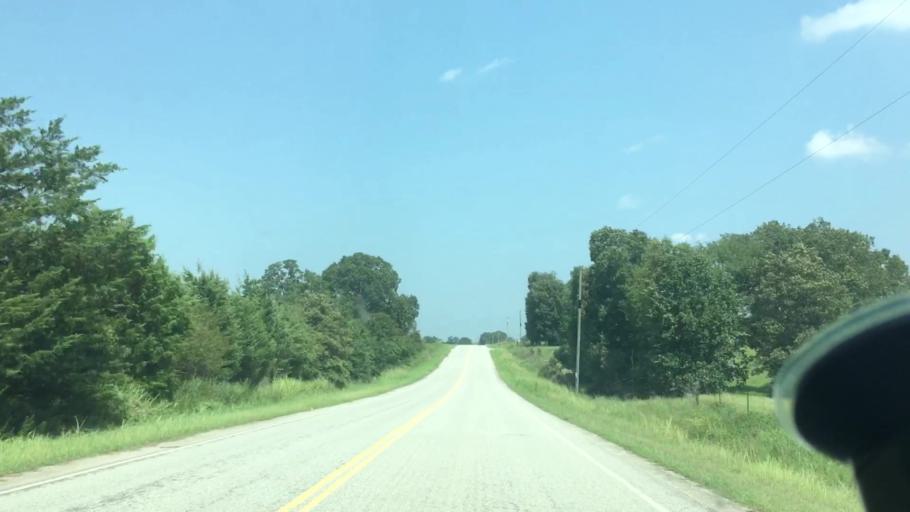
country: US
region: Oklahoma
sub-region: Atoka County
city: Atoka
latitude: 34.2699
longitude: -95.9361
